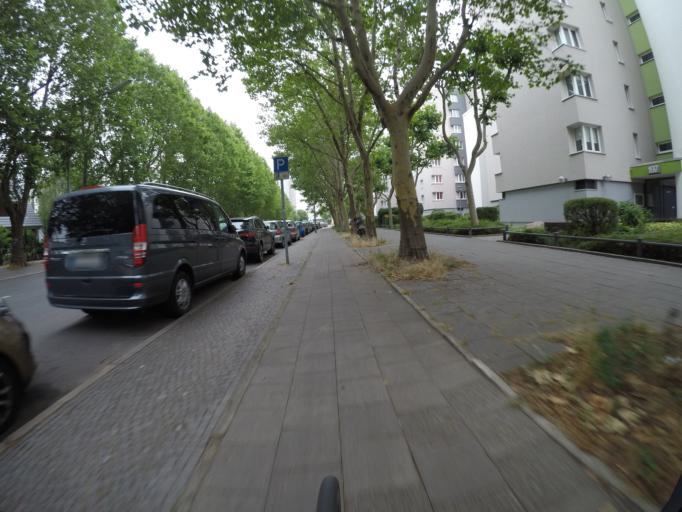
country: DE
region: Berlin
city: Markisches Viertel
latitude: 52.5960
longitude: 13.3451
